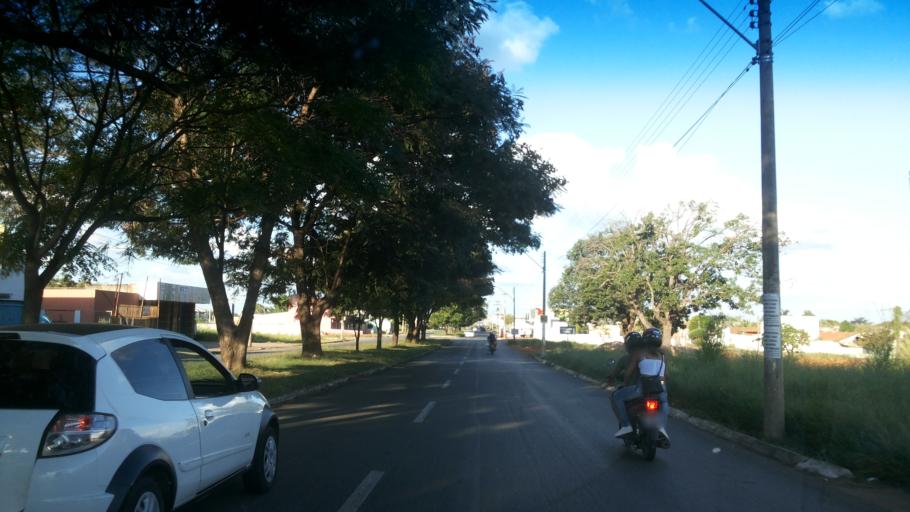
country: BR
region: Goias
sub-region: Goiania
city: Goiania
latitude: -16.7496
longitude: -49.3296
